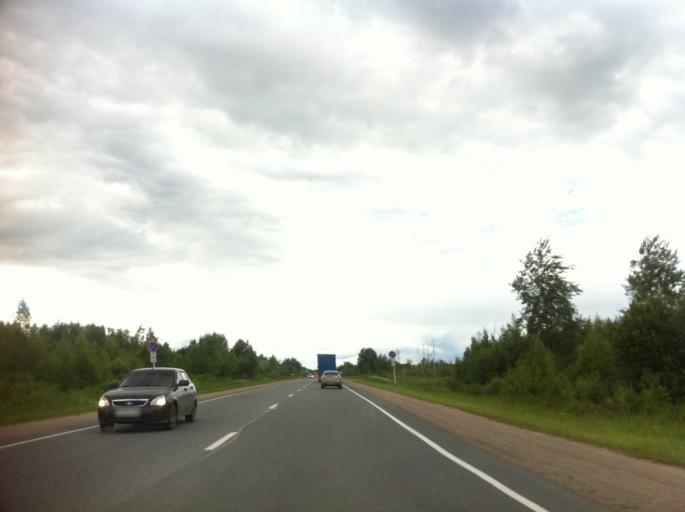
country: RU
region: Pskov
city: Pskov
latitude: 57.8432
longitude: 28.3970
